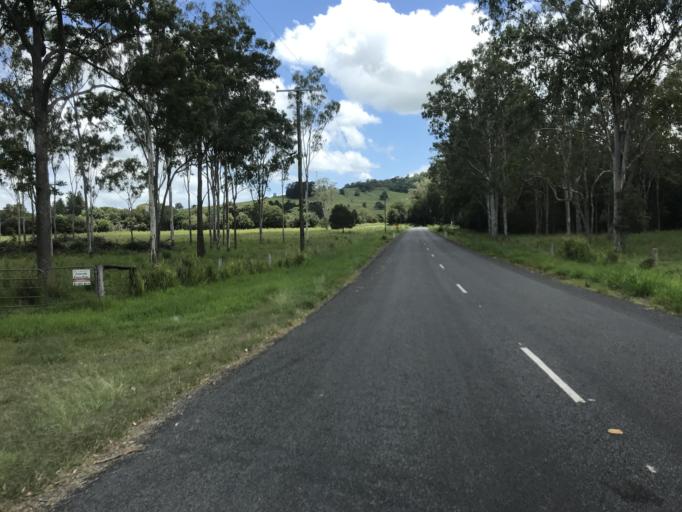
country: AU
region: Queensland
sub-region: Tablelands
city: Atherton
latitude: -17.3009
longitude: 145.5595
